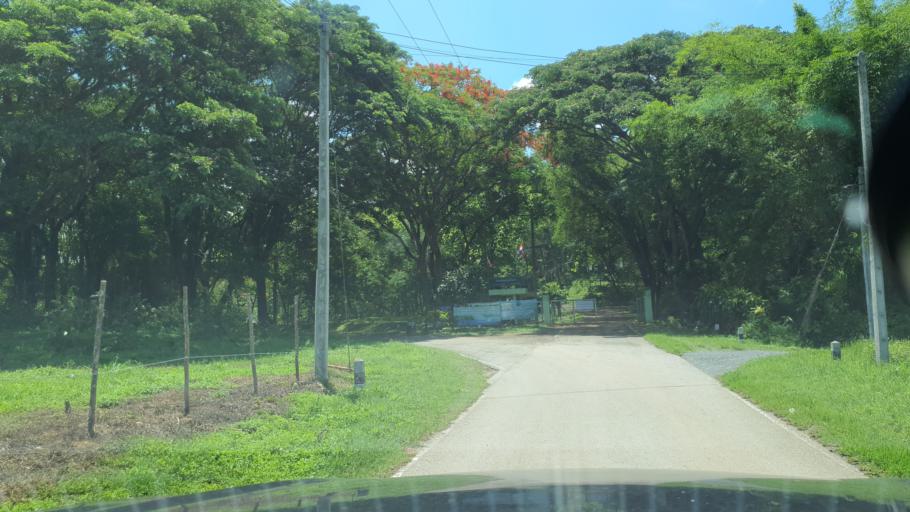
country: TH
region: Chiang Mai
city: Mae On
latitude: 18.8141
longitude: 99.2625
